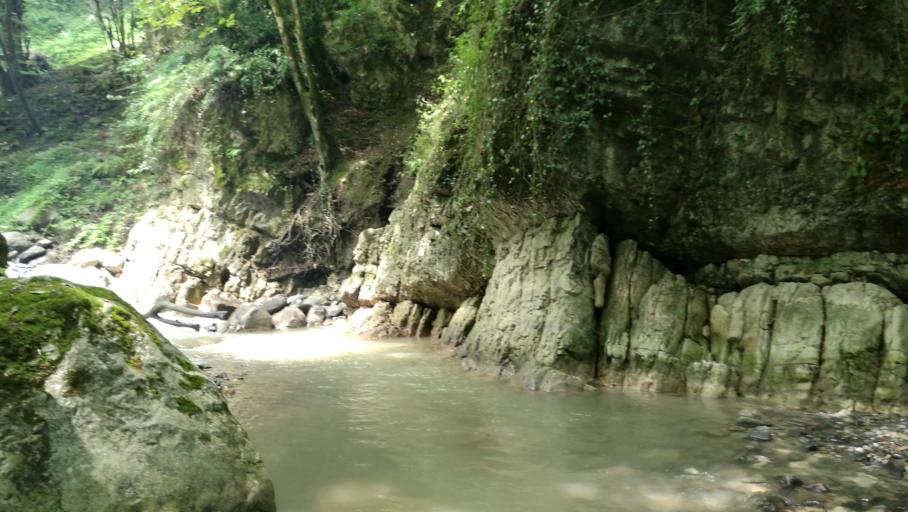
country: IR
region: Mazandaran
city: Ramsar
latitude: 36.8871
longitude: 50.5719
